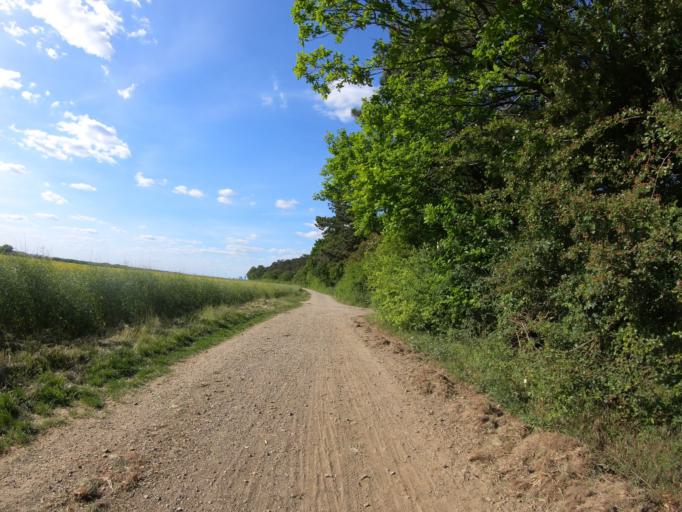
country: DE
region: Lower Saxony
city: Leiferde
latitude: 52.1876
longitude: 10.5285
